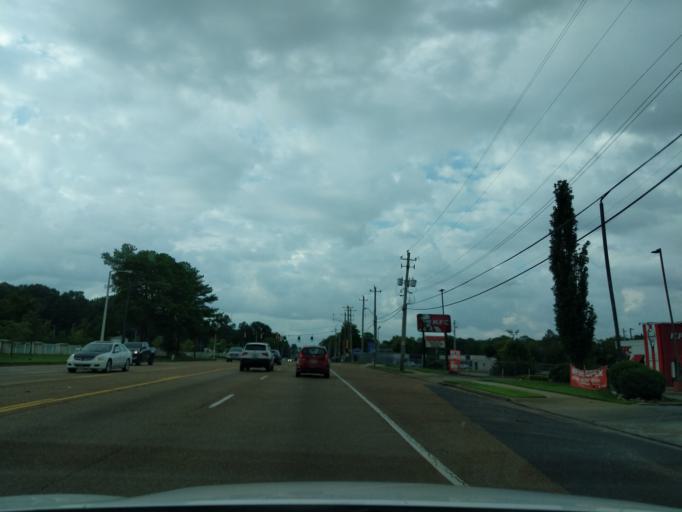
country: US
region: Tennessee
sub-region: Shelby County
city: New South Memphis
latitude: 35.0504
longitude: -90.0252
